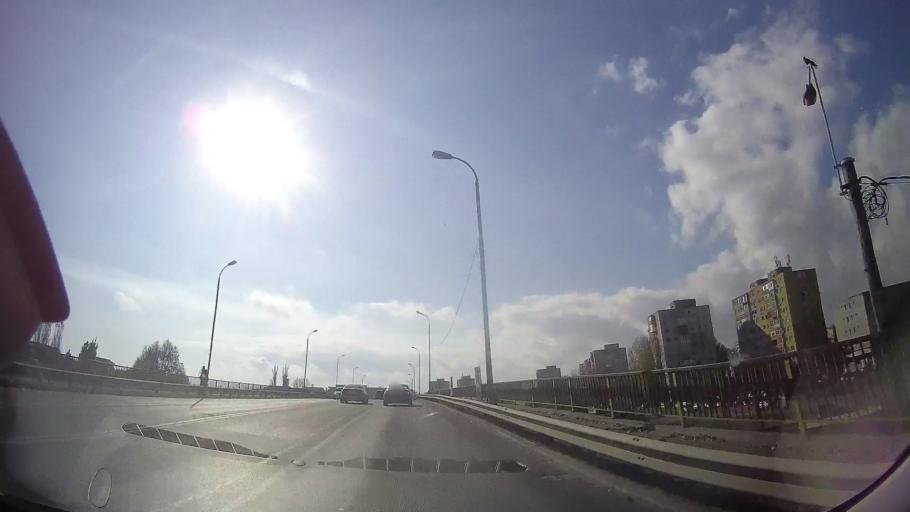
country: RO
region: Constanta
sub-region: Municipiul Constanta
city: Constanta
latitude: 44.1493
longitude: 28.6263
